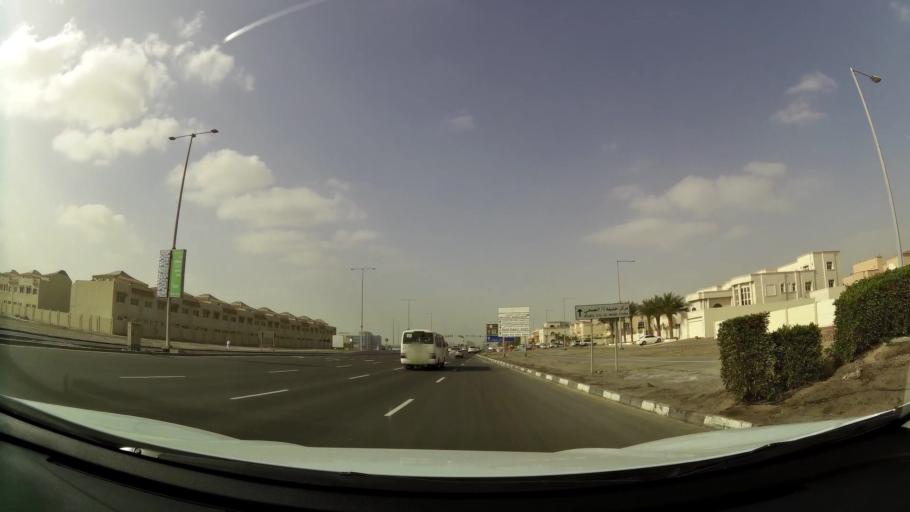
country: AE
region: Abu Dhabi
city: Abu Dhabi
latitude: 24.4018
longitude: 54.5729
